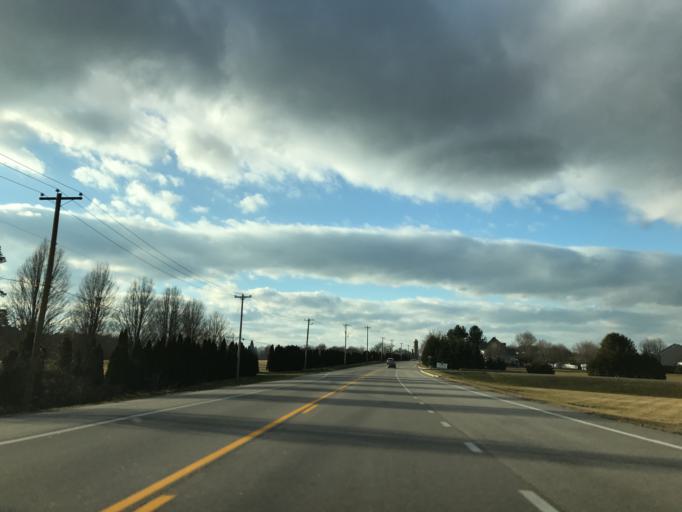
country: US
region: Maryland
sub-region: Cecil County
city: North East
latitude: 39.6574
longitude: -75.9943
